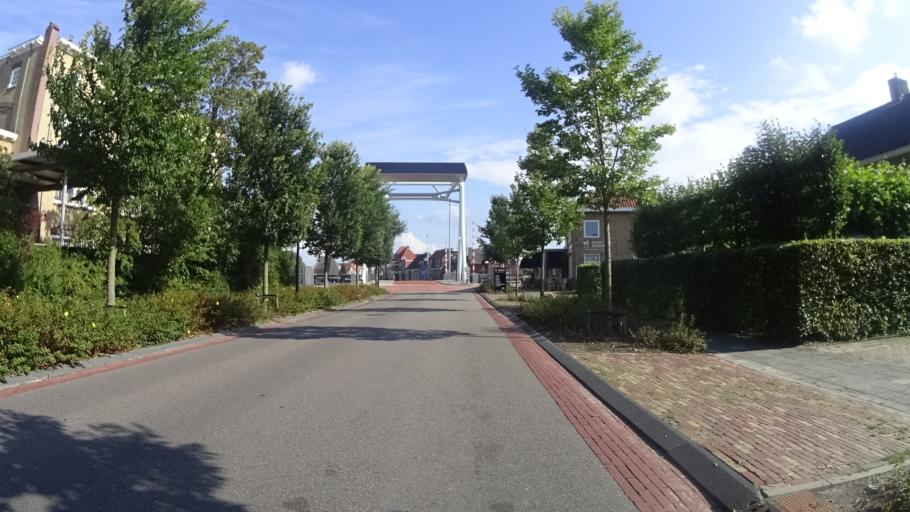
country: NL
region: Friesland
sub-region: Gemeente Franekeradeel
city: Franeker
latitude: 53.1837
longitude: 5.5485
